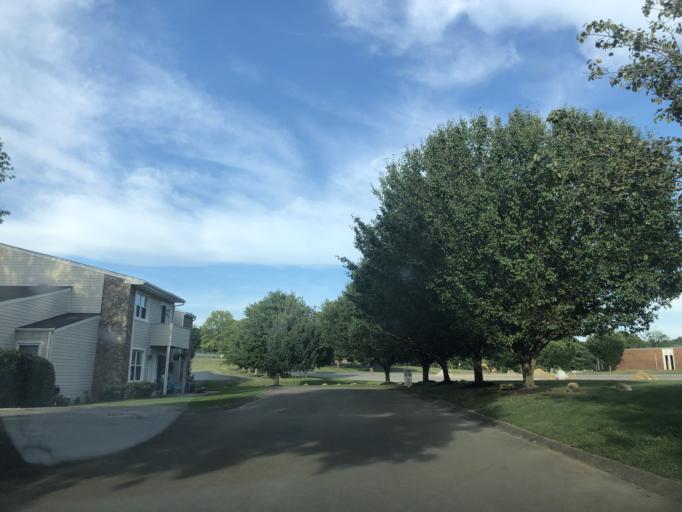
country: US
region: Tennessee
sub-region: Davidson County
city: Belle Meade
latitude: 36.0717
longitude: -86.9365
